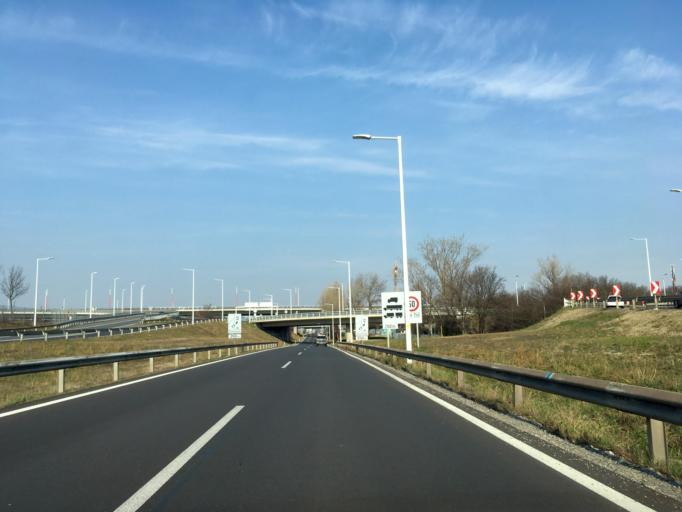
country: AT
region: Vienna
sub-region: Wien Stadt
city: Vienna
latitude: 48.2085
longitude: 16.4446
